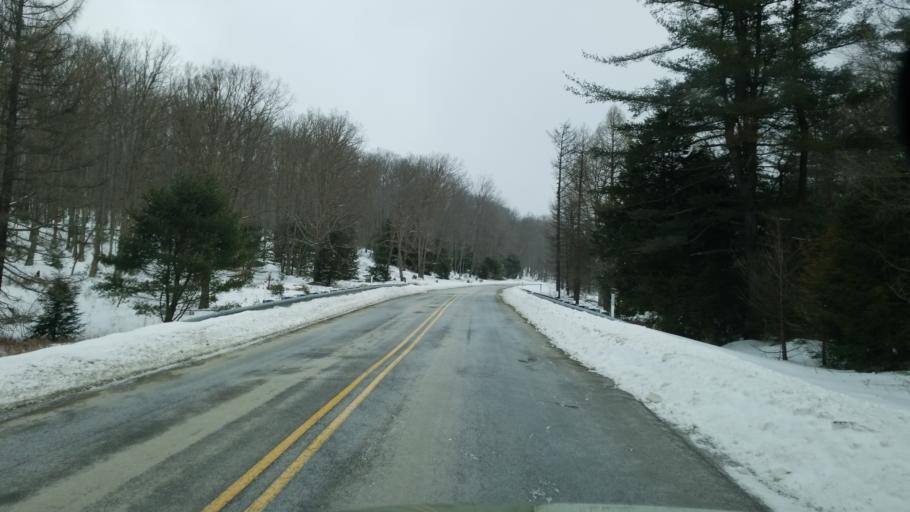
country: US
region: Pennsylvania
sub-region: Clearfield County
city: Shiloh
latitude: 41.2358
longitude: -78.1883
